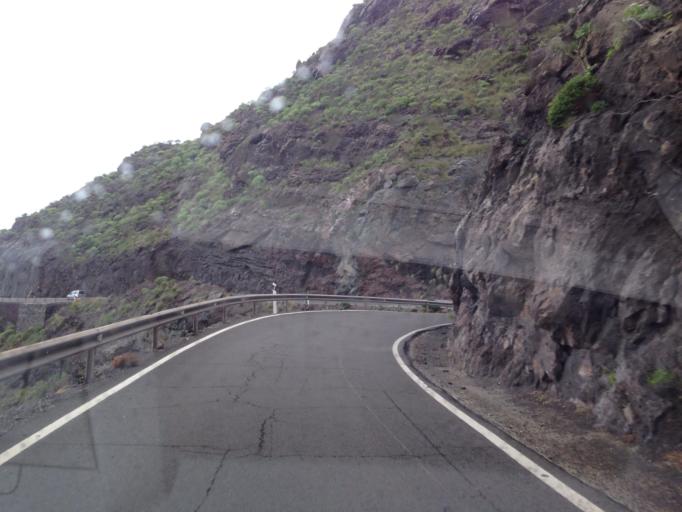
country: ES
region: Canary Islands
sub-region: Provincia de Las Palmas
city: San Nicolas
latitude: 28.0366
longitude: -15.7498
